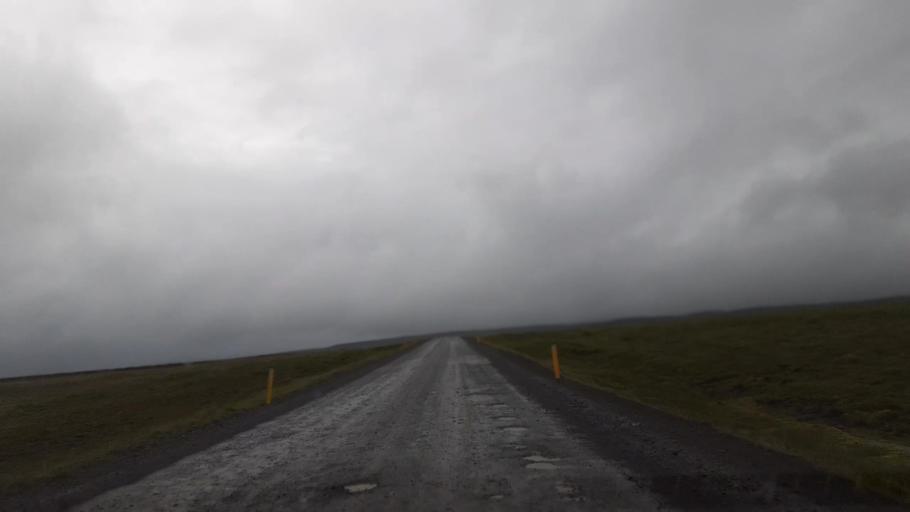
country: IS
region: East
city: Egilsstadir
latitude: 66.0358
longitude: -15.0695
